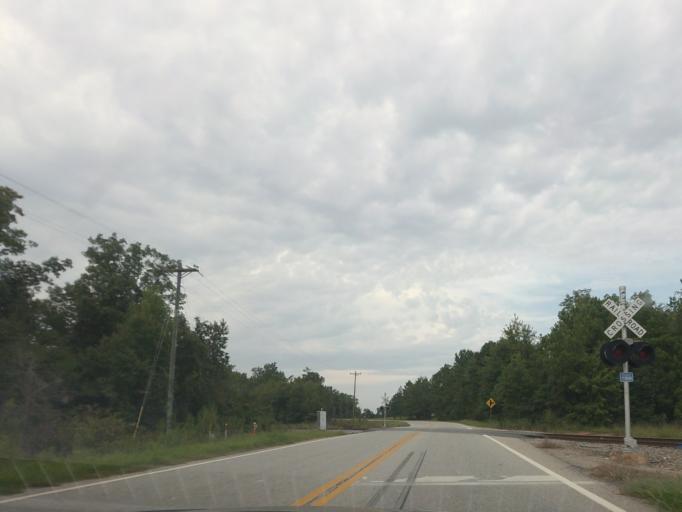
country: US
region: Georgia
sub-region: Twiggs County
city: Jeffersonville
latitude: 32.7575
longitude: -83.4439
